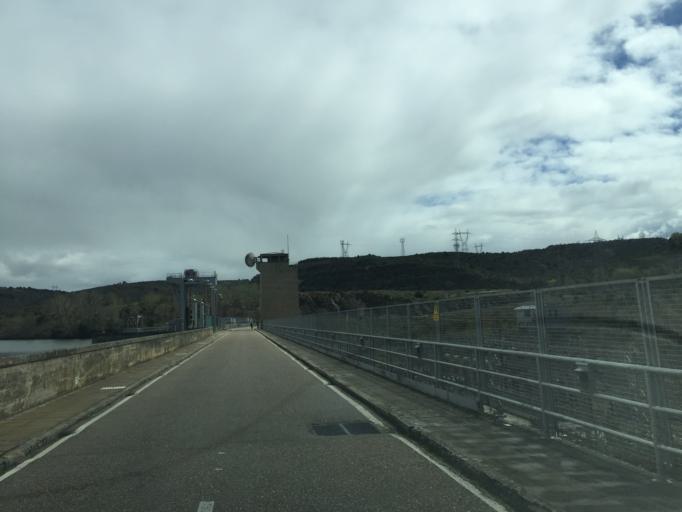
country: ES
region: Castille and Leon
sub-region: Provincia de Zamora
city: Moral de Sayago
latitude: 41.4916
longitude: -6.0873
